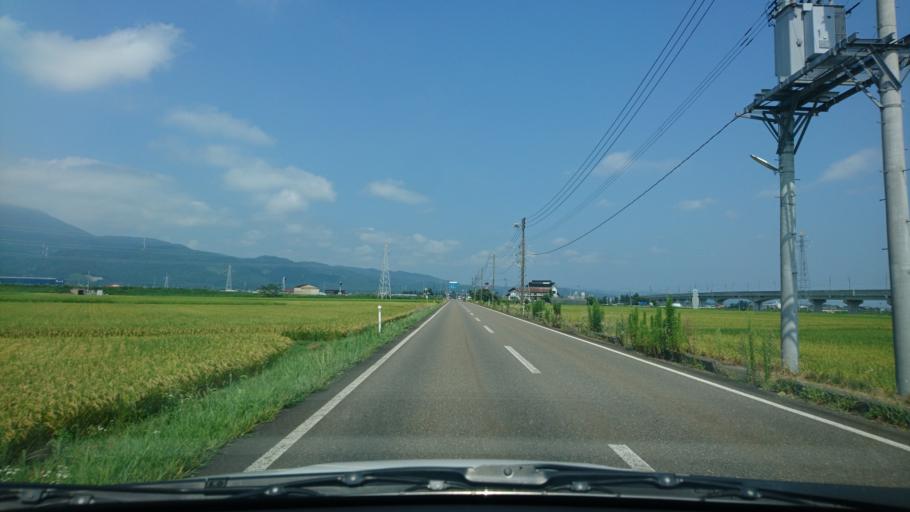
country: JP
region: Niigata
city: Arai
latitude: 37.0634
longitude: 138.2663
